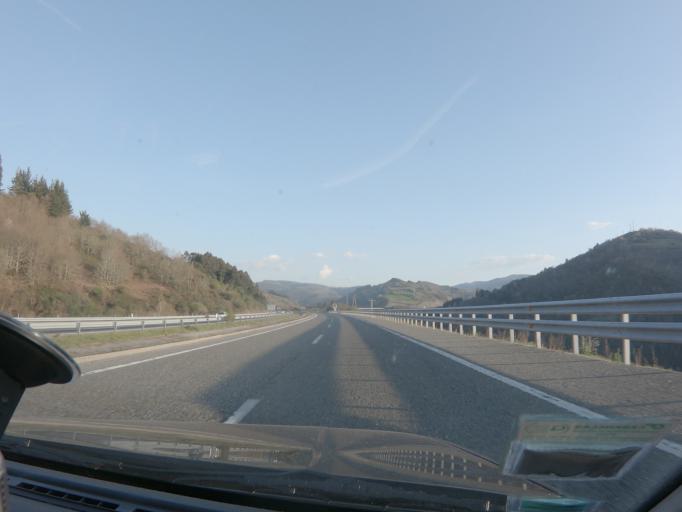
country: ES
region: Galicia
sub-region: Provincia de Lugo
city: Becerrea
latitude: 42.8259
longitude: -7.1171
